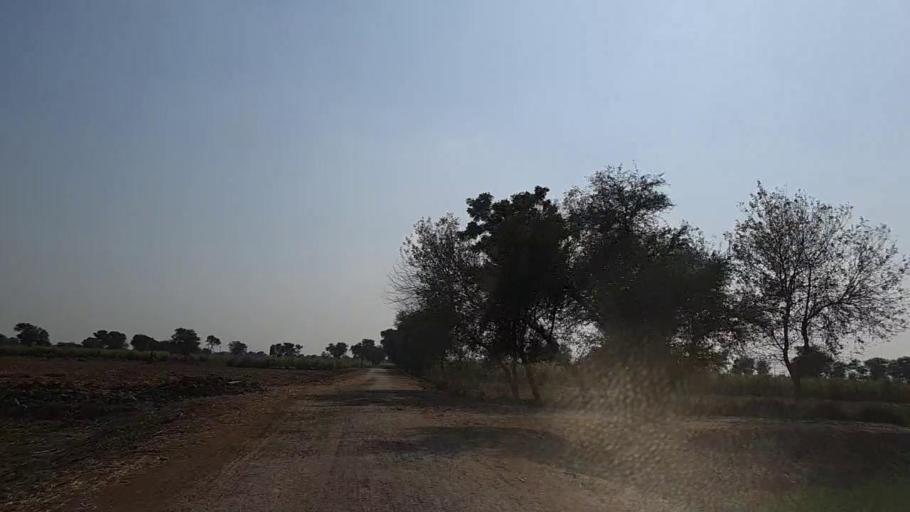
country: PK
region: Sindh
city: Daur
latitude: 26.4376
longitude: 68.2332
